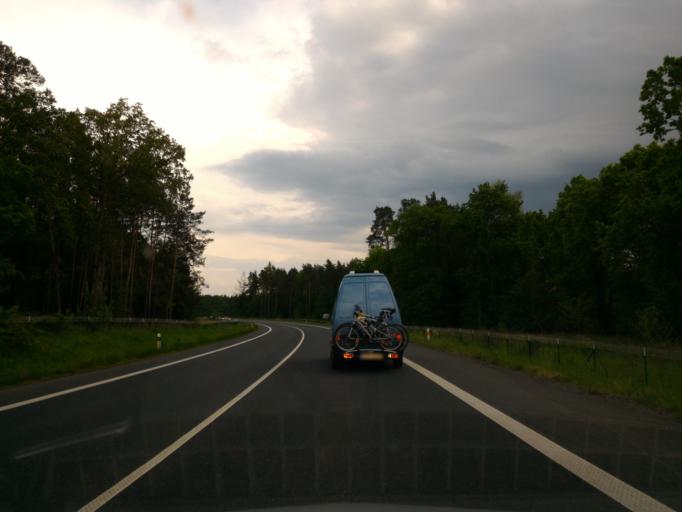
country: CZ
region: Central Bohemia
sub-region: Okres Nymburk
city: Nymburk
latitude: 50.1824
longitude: 15.0787
